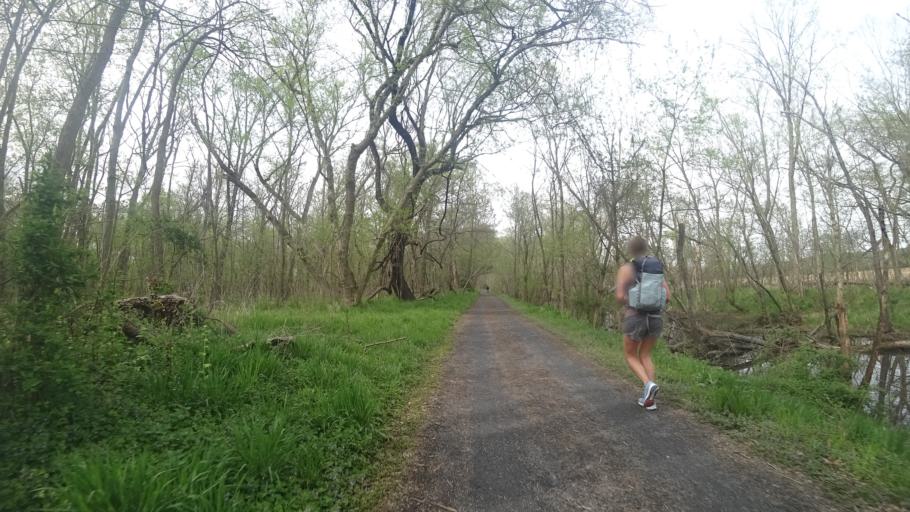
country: US
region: Virginia
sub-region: Loudoun County
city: Leesburg
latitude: 39.1644
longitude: -77.5153
